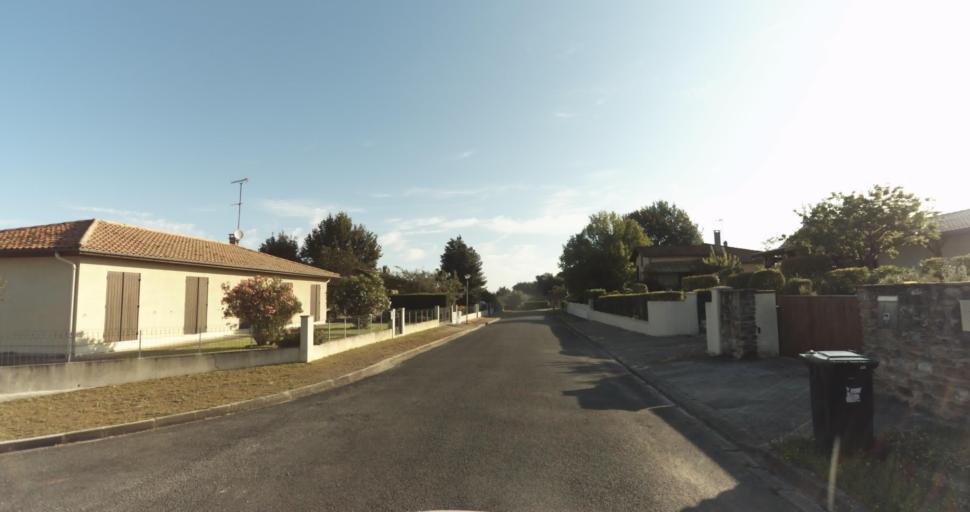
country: FR
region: Aquitaine
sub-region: Departement de la Gironde
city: Bazas
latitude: 44.4243
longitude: -0.2194
